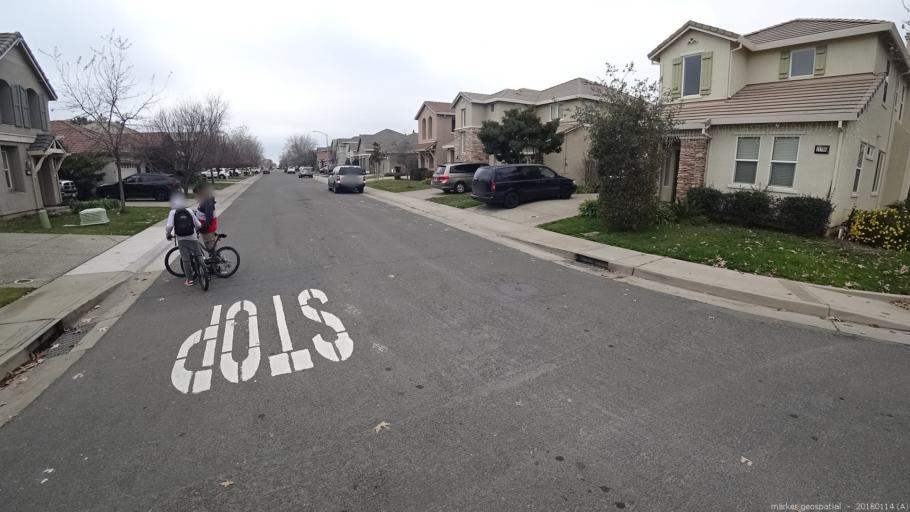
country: US
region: California
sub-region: Sacramento County
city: Rancho Cordova
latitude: 38.5531
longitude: -121.2388
